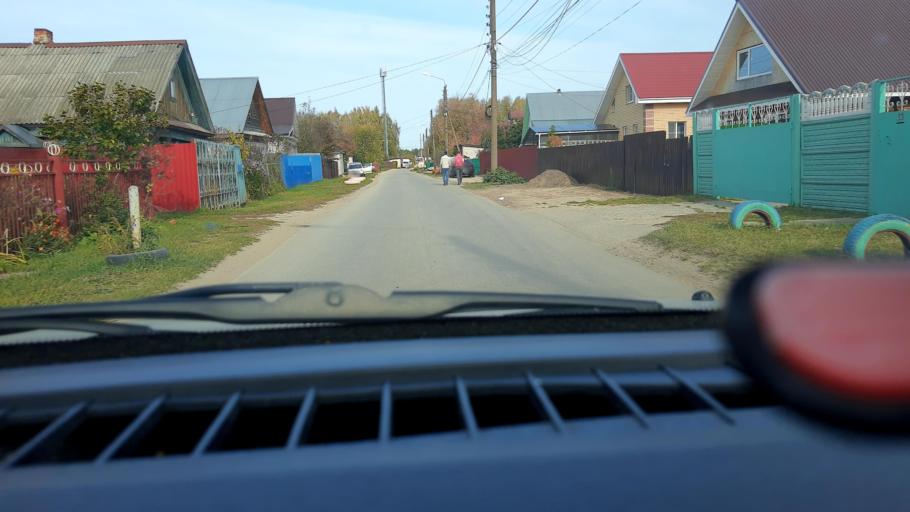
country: RU
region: Nizjnij Novgorod
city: Afonino
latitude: 56.2973
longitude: 44.1937
